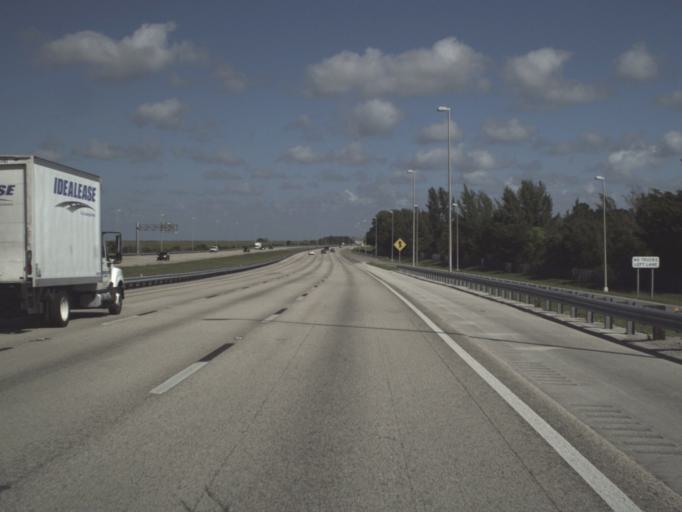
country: US
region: Florida
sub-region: Broward County
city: Coral Springs
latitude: 26.2756
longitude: -80.2965
